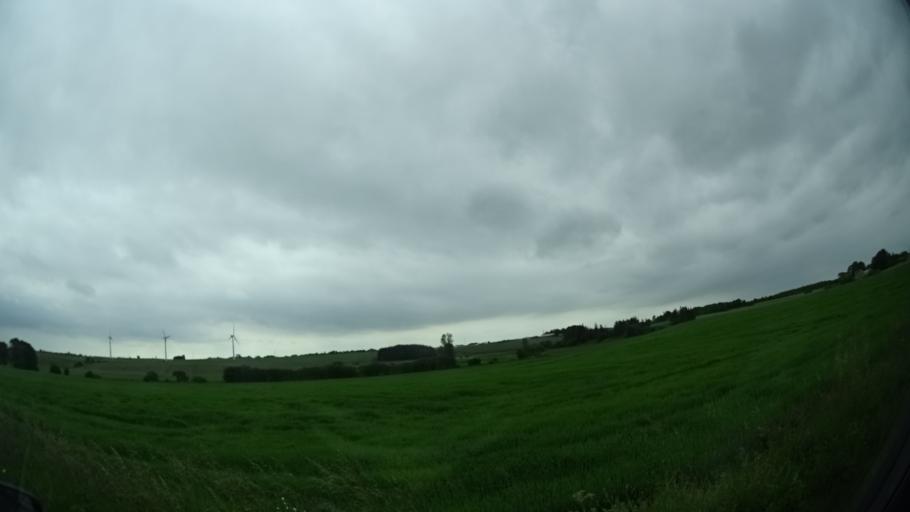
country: DK
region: Central Jutland
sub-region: Arhus Kommune
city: Solbjerg
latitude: 56.0769
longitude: 10.0876
